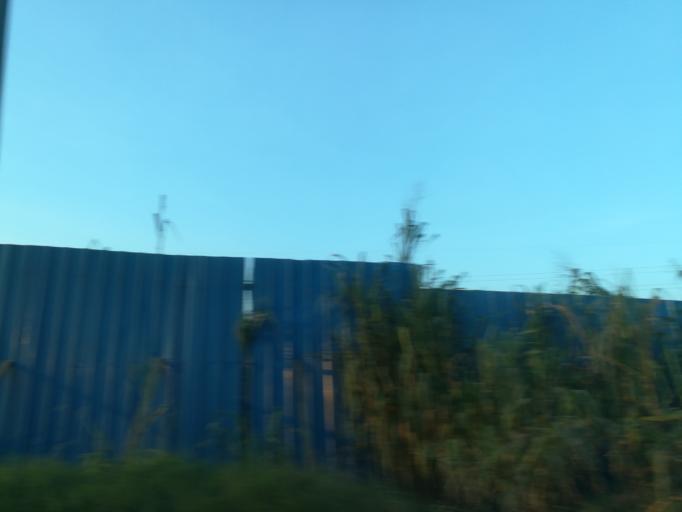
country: NG
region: Lagos
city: Ebute Ikorodu
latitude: 6.6188
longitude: 3.4602
